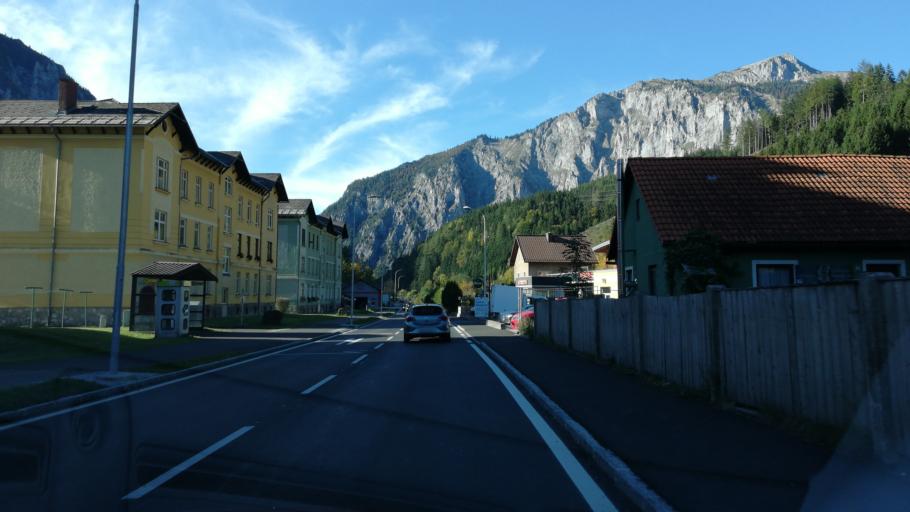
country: AT
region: Styria
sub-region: Politischer Bezirk Leoben
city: Eisenerz
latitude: 47.5570
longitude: 14.8698
